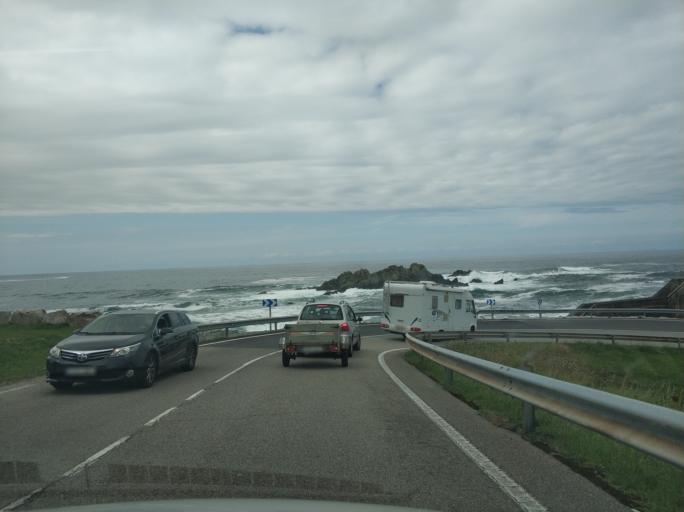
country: ES
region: Asturias
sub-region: Province of Asturias
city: Cudillero
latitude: 43.5677
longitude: -6.1538
